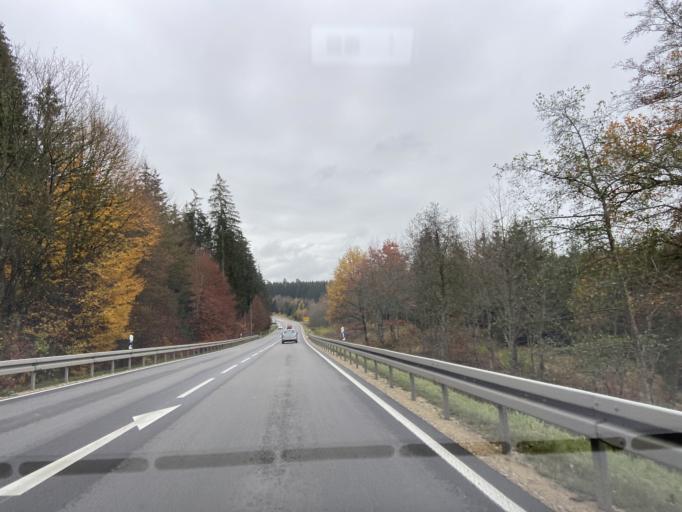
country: DE
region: Baden-Wuerttemberg
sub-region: Tuebingen Region
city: Krauchenwies
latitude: 48.0482
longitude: 9.2360
